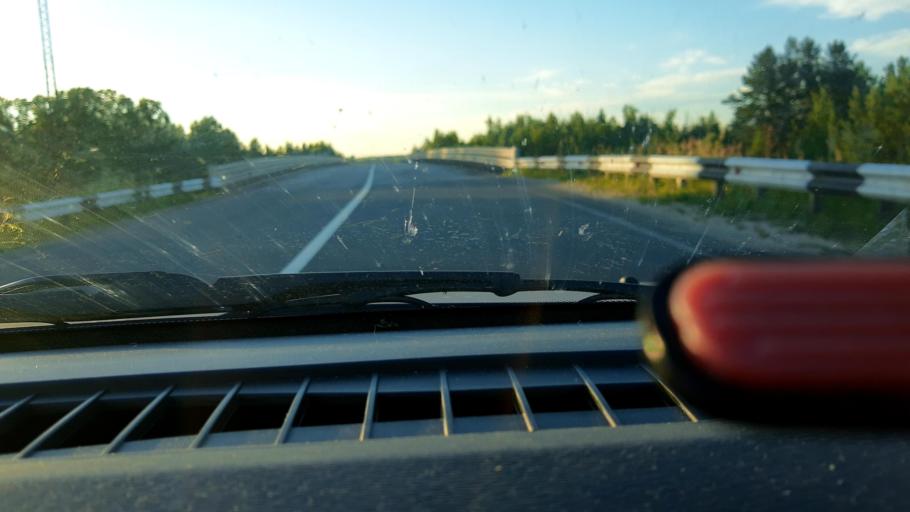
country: RU
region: Nizjnij Novgorod
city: Uren'
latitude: 57.4390
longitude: 45.7148
